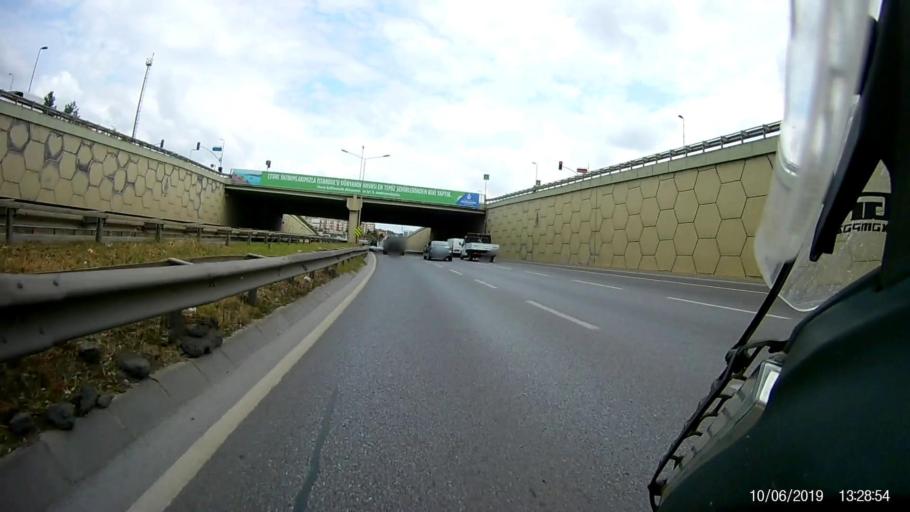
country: TR
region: Istanbul
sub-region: Atasehir
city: Atasehir
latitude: 40.9598
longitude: 29.1022
